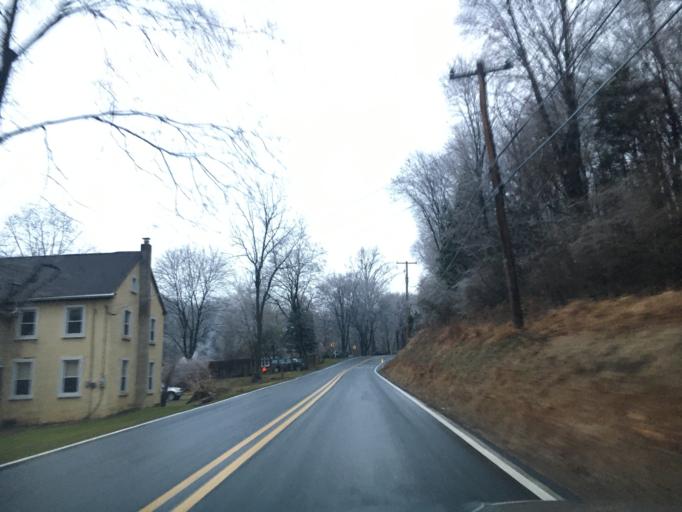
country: US
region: Pennsylvania
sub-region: Lehigh County
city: Schnecksville
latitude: 40.6384
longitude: -75.5984
